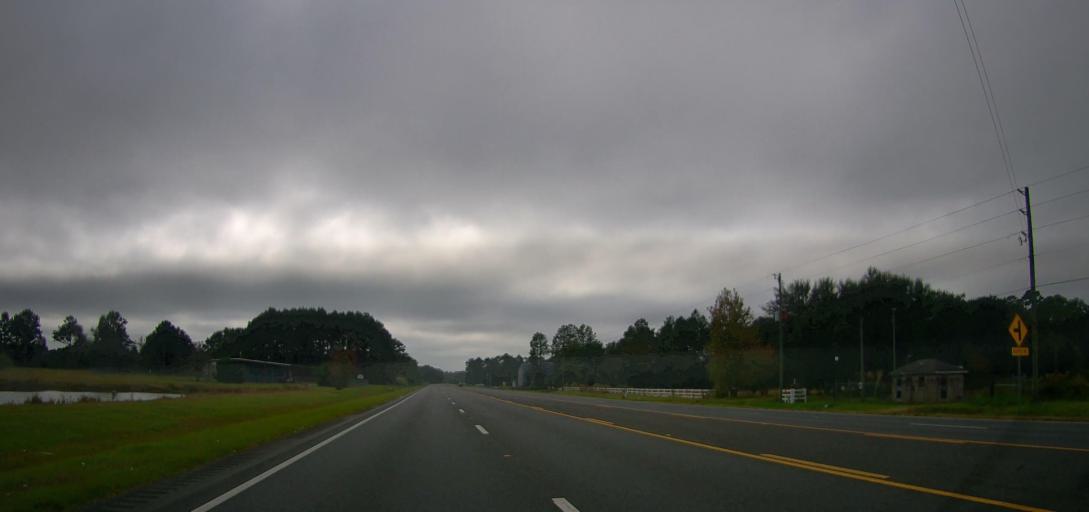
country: US
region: Georgia
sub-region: Thomas County
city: Thomasville
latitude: 30.9906
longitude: -83.8761
